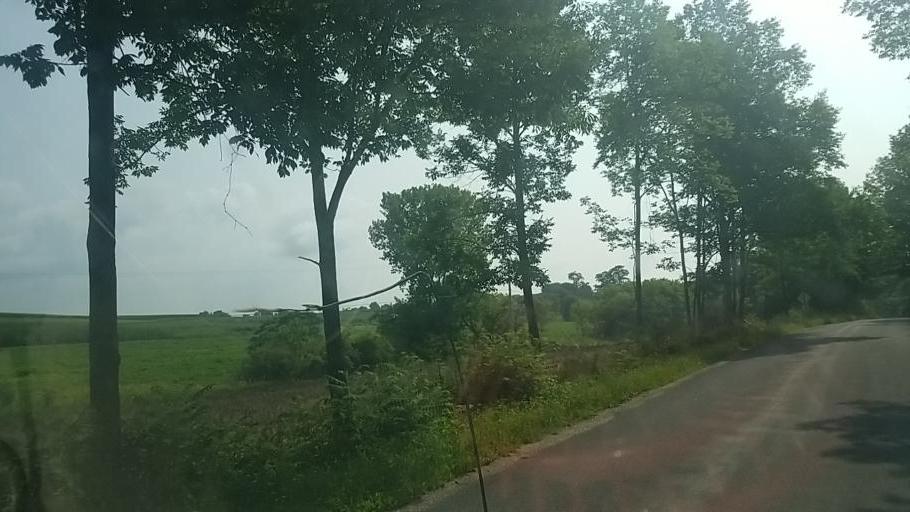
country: US
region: New York
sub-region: Montgomery County
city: Fonda
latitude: 42.9761
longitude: -74.4439
